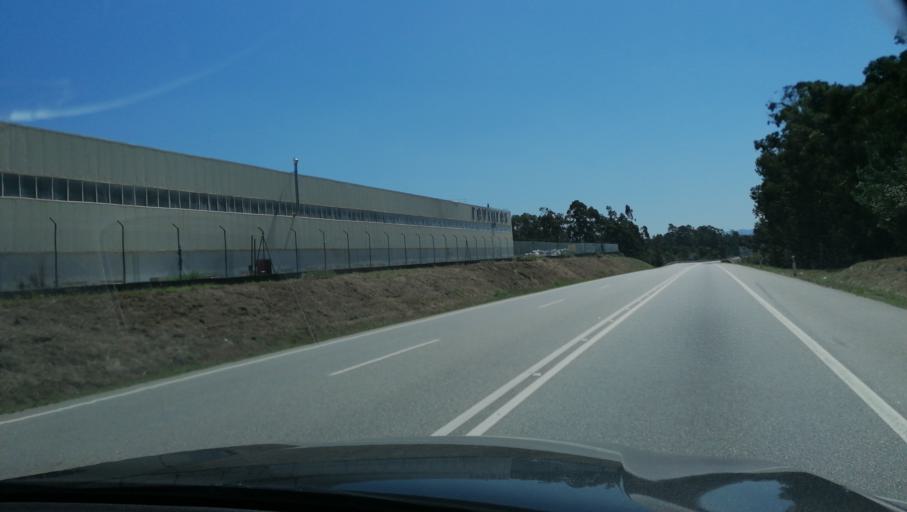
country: PT
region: Aveiro
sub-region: Agueda
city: Aguada de Cima
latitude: 40.5311
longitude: -8.4563
